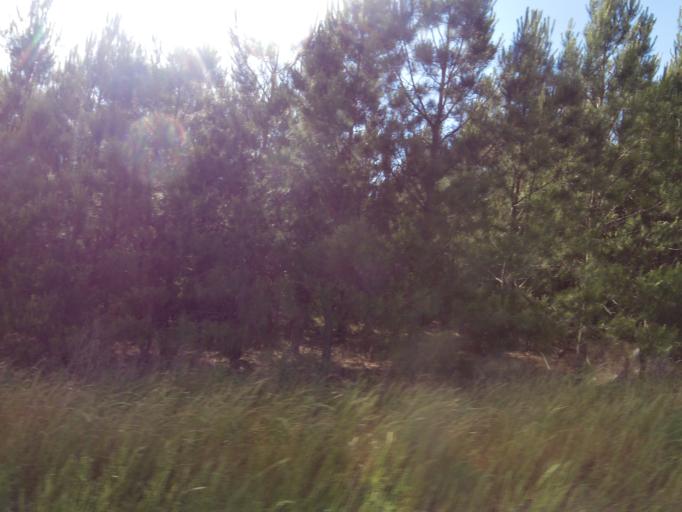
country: US
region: South Carolina
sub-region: Allendale County
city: Fairfax
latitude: 32.9825
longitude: -81.2269
